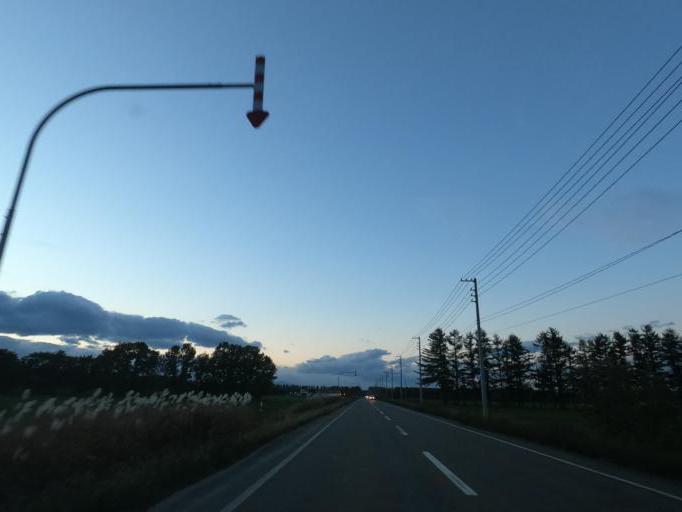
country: JP
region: Hokkaido
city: Obihiro
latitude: 42.6665
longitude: 143.1754
